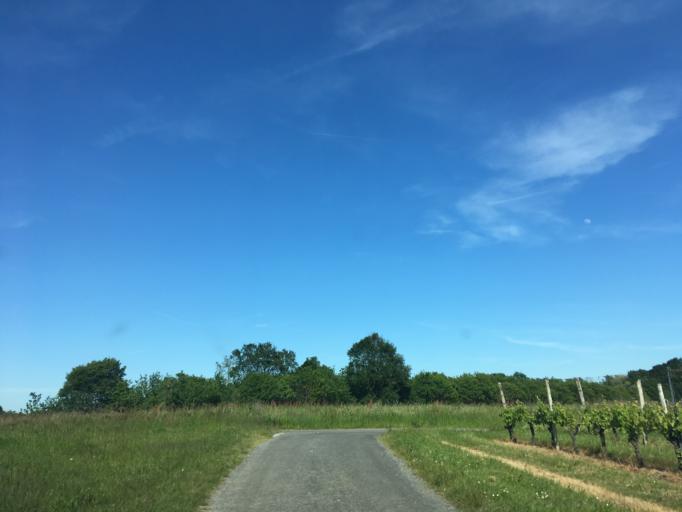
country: FR
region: Poitou-Charentes
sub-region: Departement de la Charente-Maritime
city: Mirambeau
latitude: 45.3384
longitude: -0.5820
